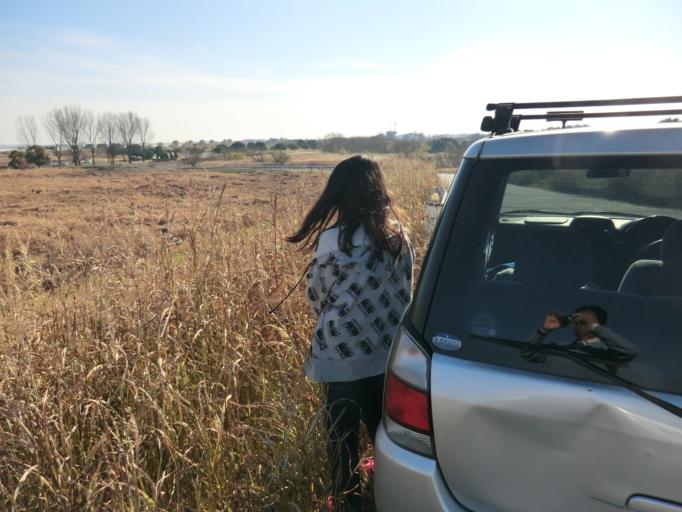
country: JP
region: Tochigi
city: Fujioka
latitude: 36.2348
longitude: 139.6543
